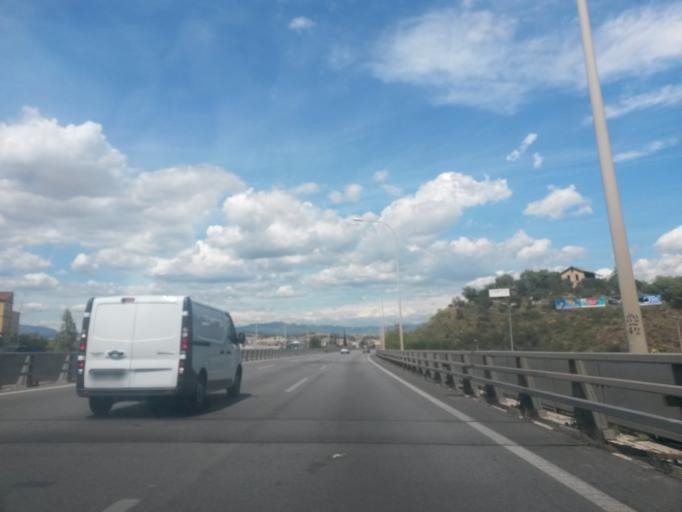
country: ES
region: Catalonia
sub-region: Provincia de Barcelona
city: Montcada i Reixac
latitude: 41.4834
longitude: 2.1844
